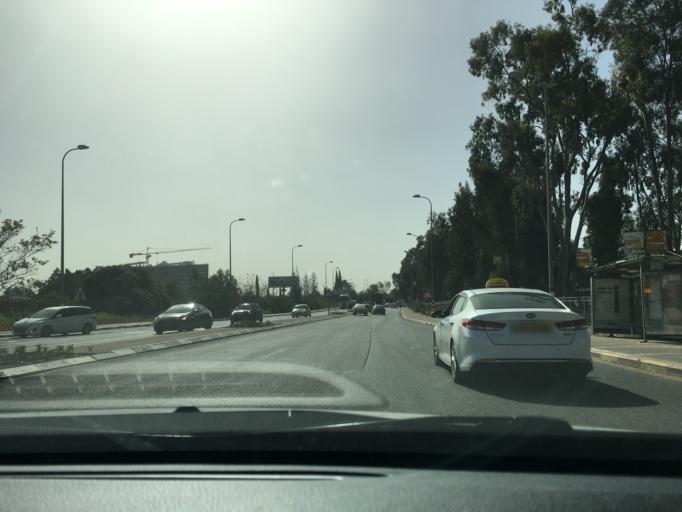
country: IL
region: Central District
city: Kfar Saba
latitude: 32.1728
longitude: 34.9312
